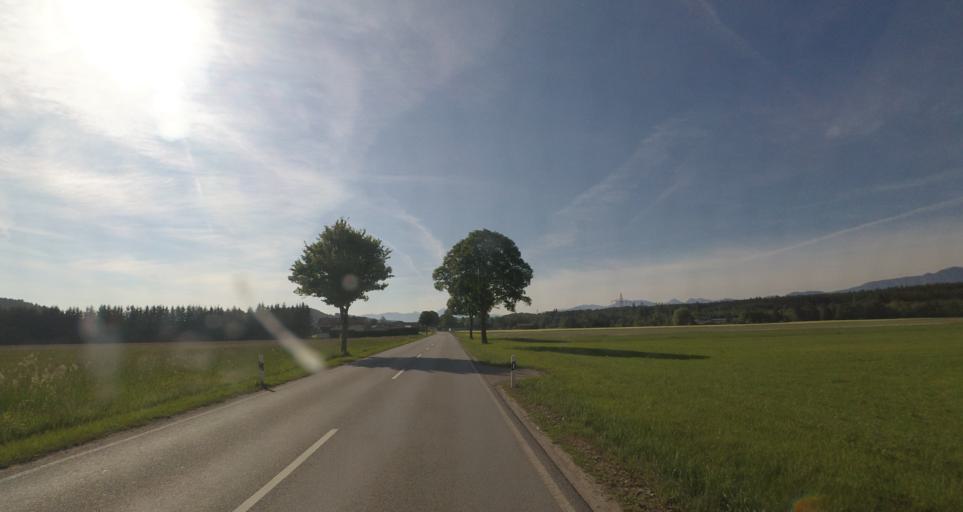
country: DE
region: Bavaria
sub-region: Upper Bavaria
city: Nussdorf
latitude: 47.8899
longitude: 12.5706
